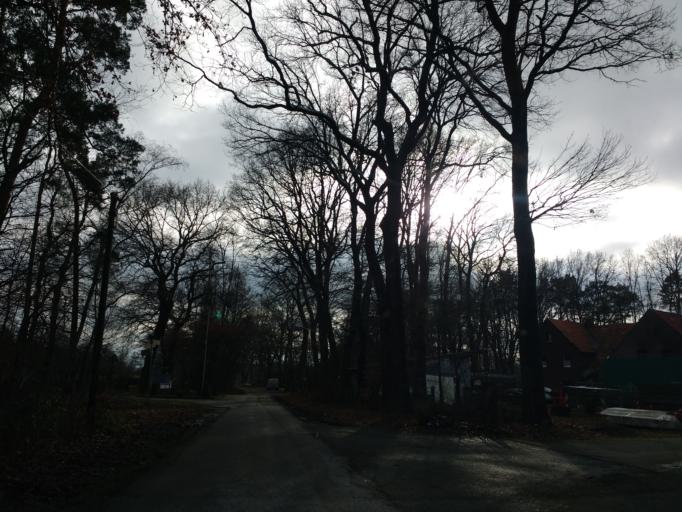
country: DE
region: North Rhine-Westphalia
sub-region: Regierungsbezirk Detmold
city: Hovelhof
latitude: 51.8101
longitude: 8.6973
